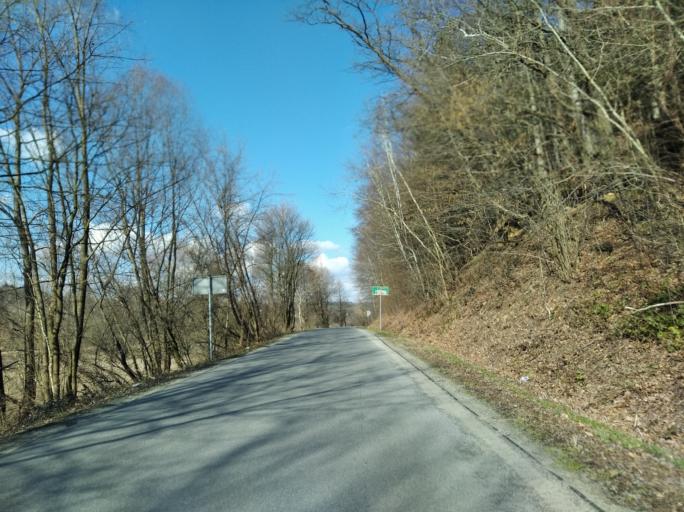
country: PL
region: Subcarpathian Voivodeship
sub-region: Powiat strzyzowski
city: Frysztak
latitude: 49.8527
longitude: 21.6245
